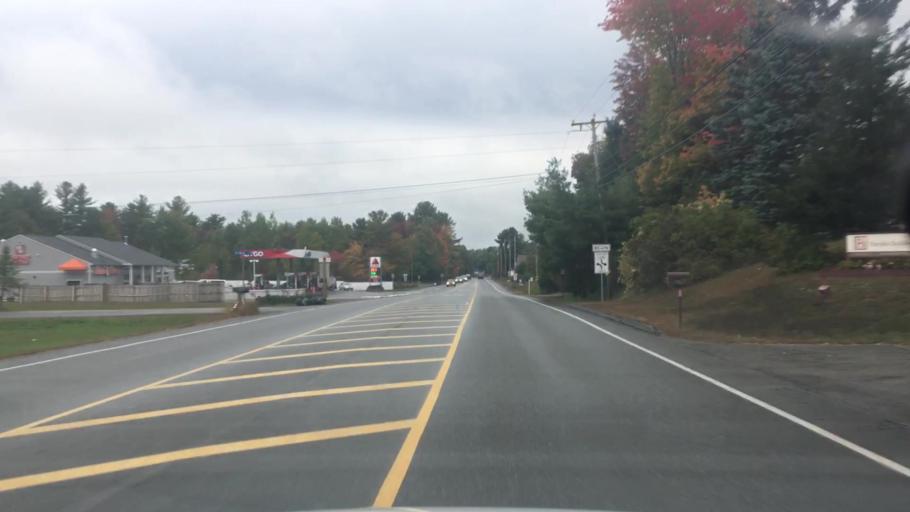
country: US
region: Maine
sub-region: Kennebec County
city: Augusta
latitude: 44.3741
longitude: -69.7957
